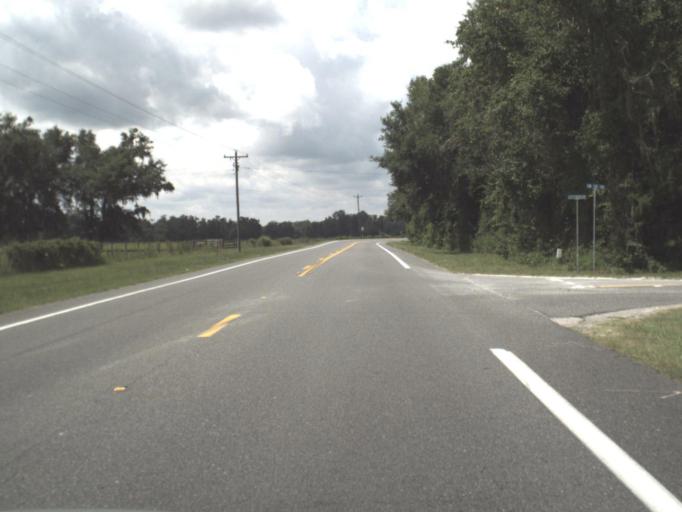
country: US
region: Florida
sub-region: Union County
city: Lake Butler
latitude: 29.9567
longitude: -82.4120
